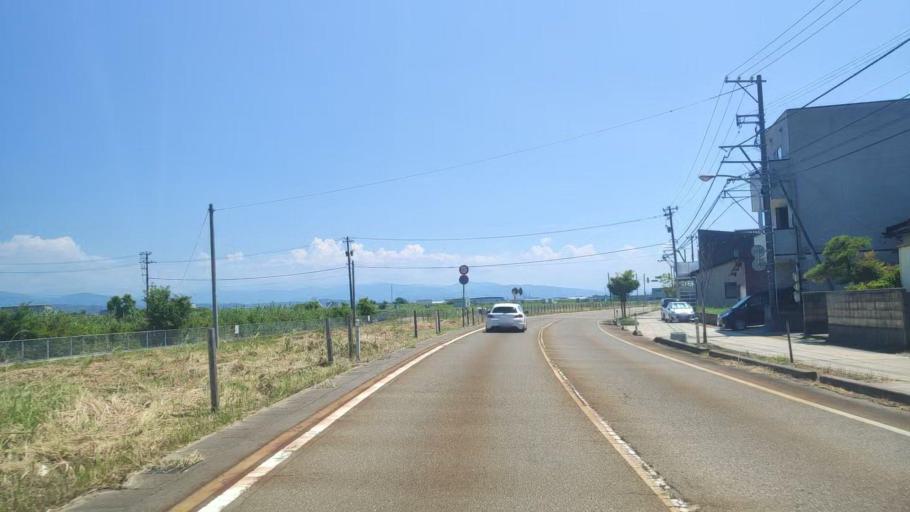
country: JP
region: Ishikawa
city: Kanazawa-shi
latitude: 36.6524
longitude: 136.6516
